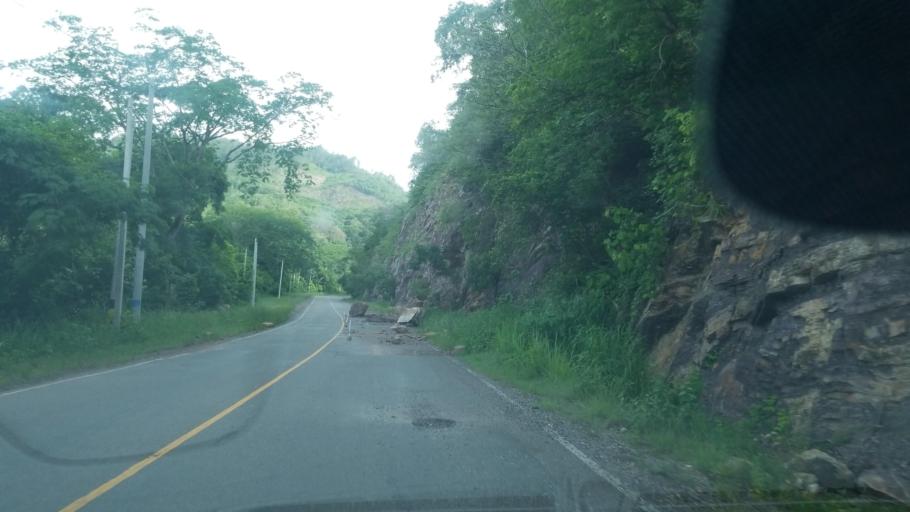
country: HN
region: Santa Barbara
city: Ilama
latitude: 15.0943
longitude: -88.2057
